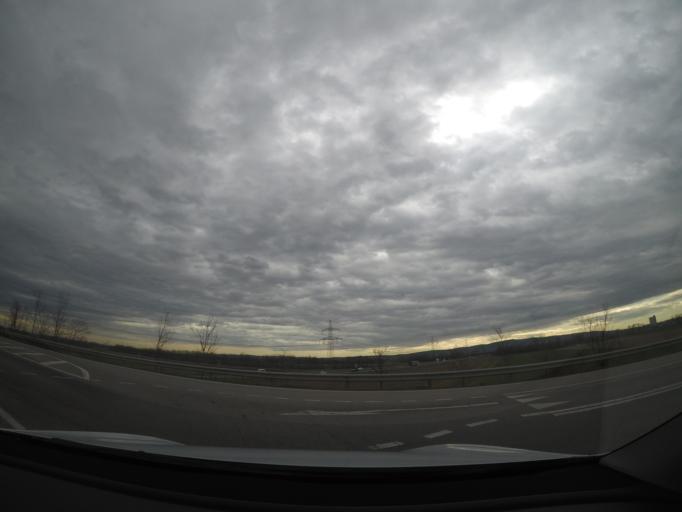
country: AT
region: Lower Austria
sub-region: Politischer Bezirk Baden
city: Ebreichsdorf
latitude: 47.9276
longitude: 16.3908
